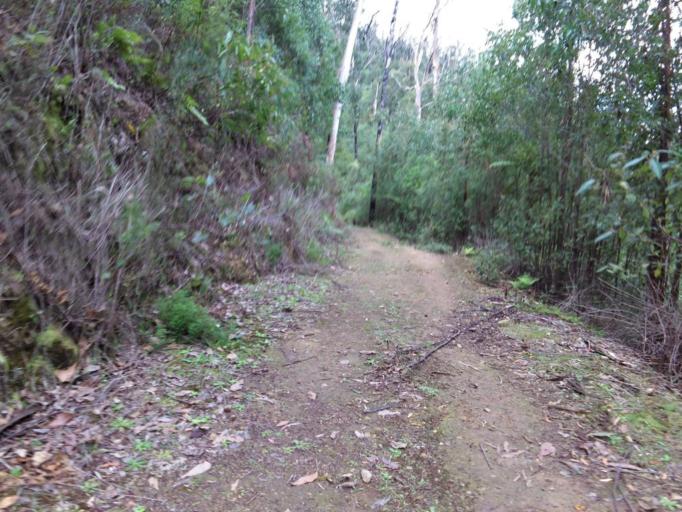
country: AU
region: Victoria
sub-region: Murrindindi
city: Kinglake West
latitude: -37.5080
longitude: 145.2359
